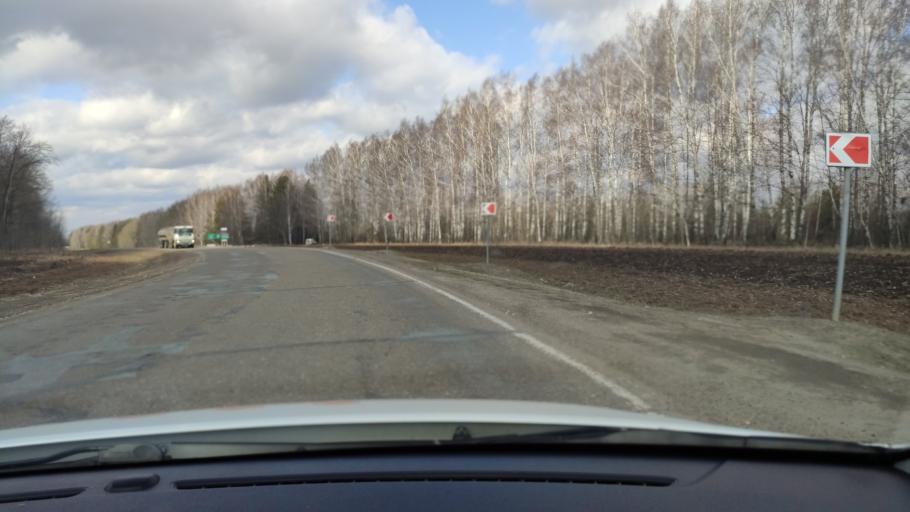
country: RU
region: Tatarstan
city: Vysokaya Gora
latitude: 56.1017
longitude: 49.1811
